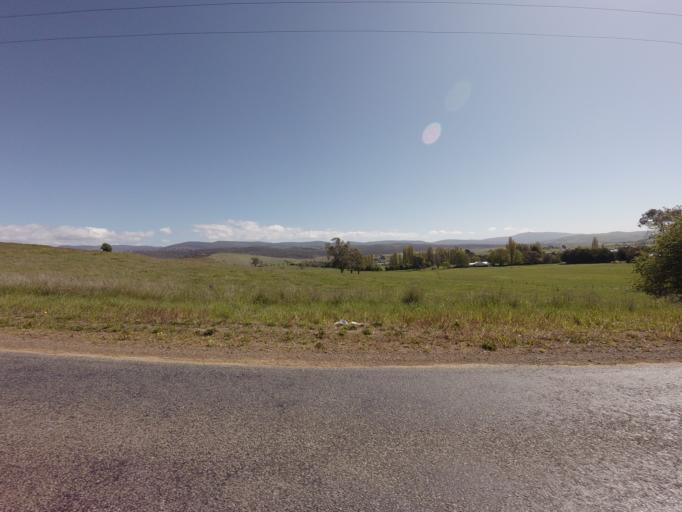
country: AU
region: Tasmania
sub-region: Derwent Valley
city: New Norfolk
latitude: -42.5363
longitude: 146.7531
